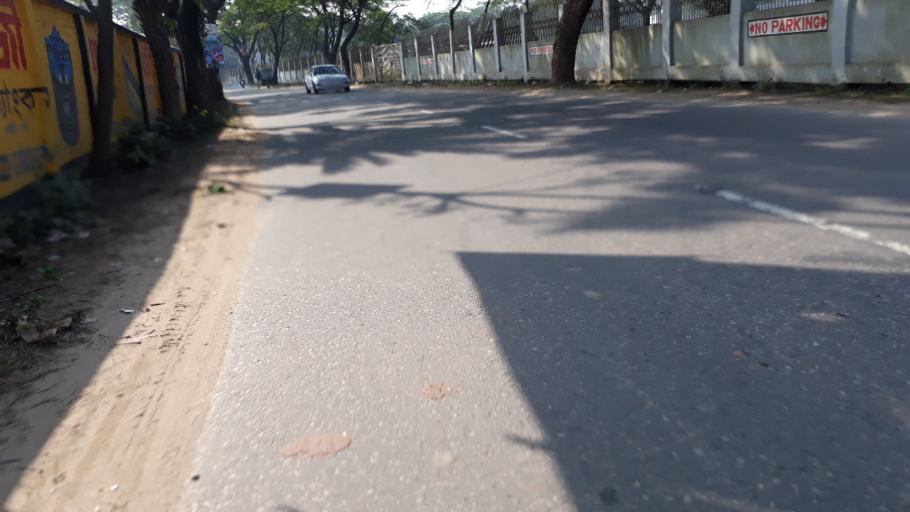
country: BD
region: Dhaka
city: Tungi
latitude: 23.9012
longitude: 90.2767
